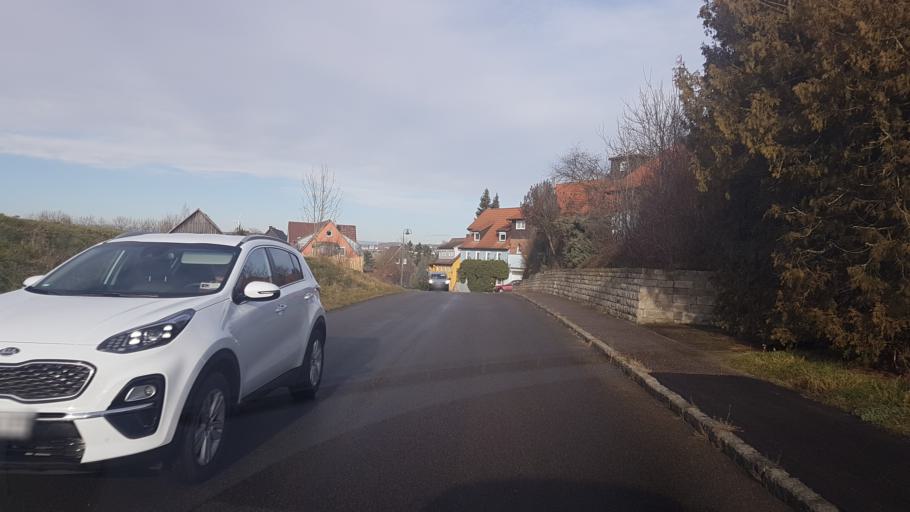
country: DE
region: Baden-Wuerttemberg
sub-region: Regierungsbezirk Stuttgart
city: Langenburg
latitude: 49.2164
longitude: 9.8843
